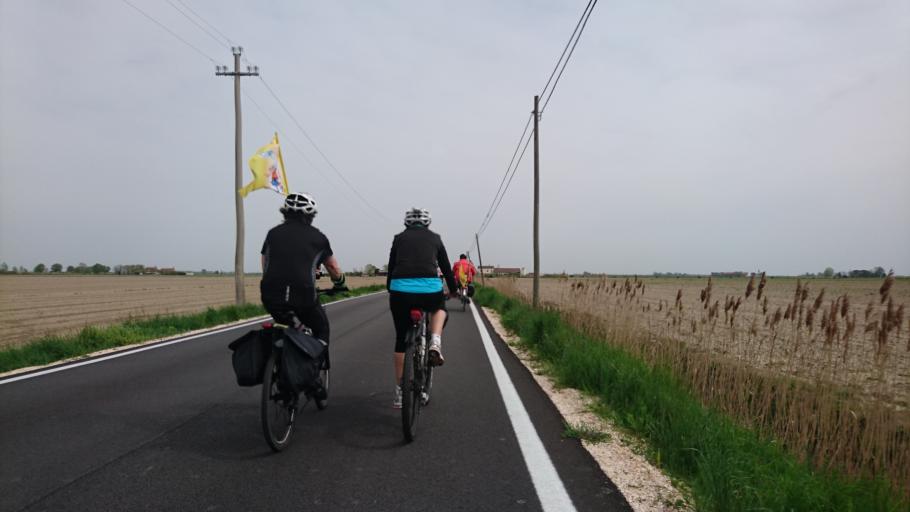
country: IT
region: Veneto
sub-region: Provincia di Venezia
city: La Salute di Livenza
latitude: 45.6570
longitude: 12.8333
